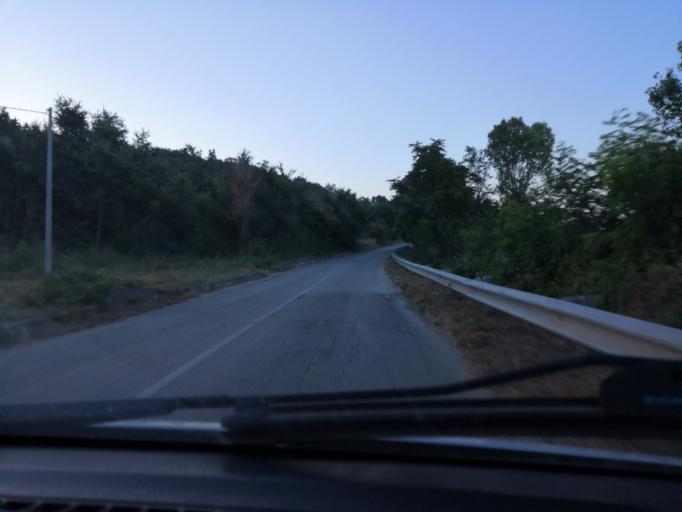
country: IT
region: Molise
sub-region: Provincia di Campobasso
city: Jelsi
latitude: 41.5183
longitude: 14.7842
